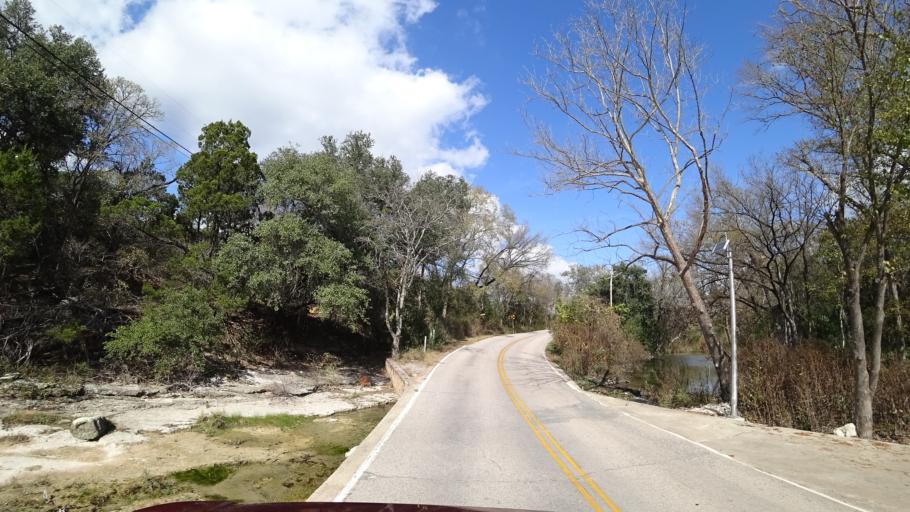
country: US
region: Texas
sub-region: Williamson County
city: Jollyville
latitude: 30.4168
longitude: -97.7952
